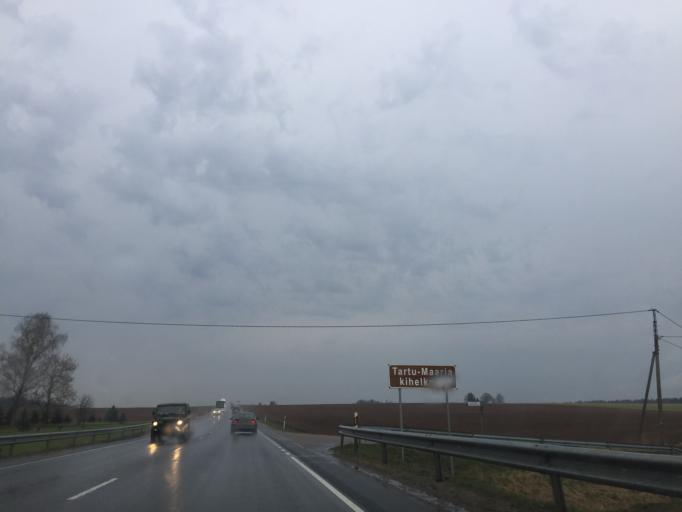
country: EE
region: Tartu
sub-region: UElenurme vald
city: Ulenurme
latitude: 58.2638
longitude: 26.6907
